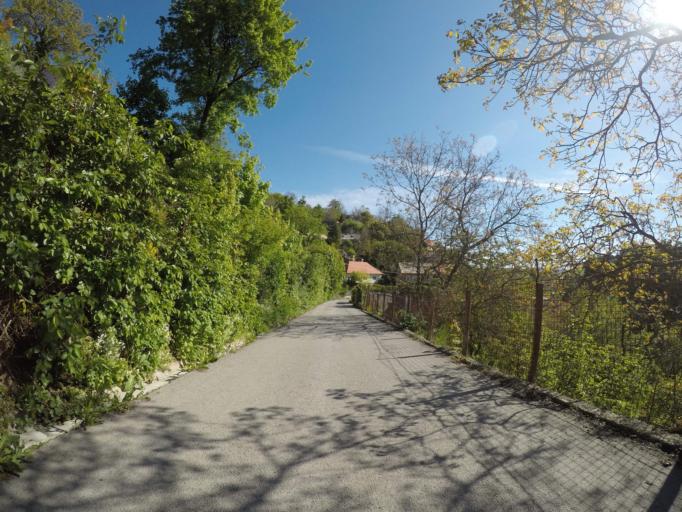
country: SK
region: Banskobystricky
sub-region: Okres Banska Bystrica
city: Banska Stiavnica
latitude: 48.4607
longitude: 18.8965
